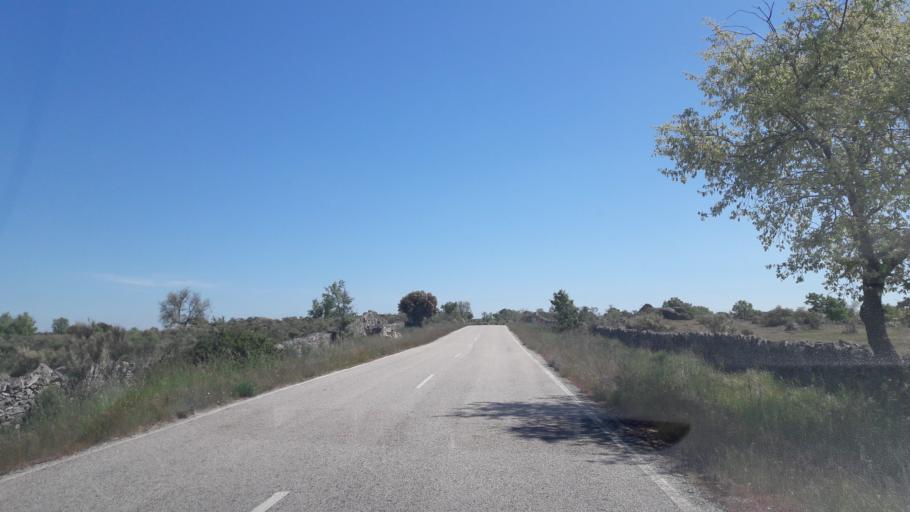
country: ES
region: Castille and Leon
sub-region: Provincia de Salamanca
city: Villarmuerto
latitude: 41.0464
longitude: -6.3863
